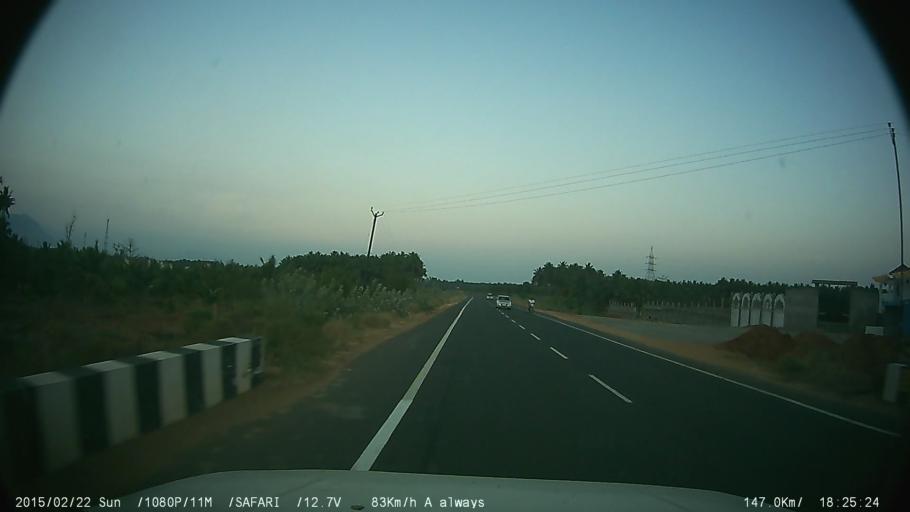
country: IN
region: Tamil Nadu
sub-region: Theni
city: Teni
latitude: 9.9569
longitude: 77.4315
